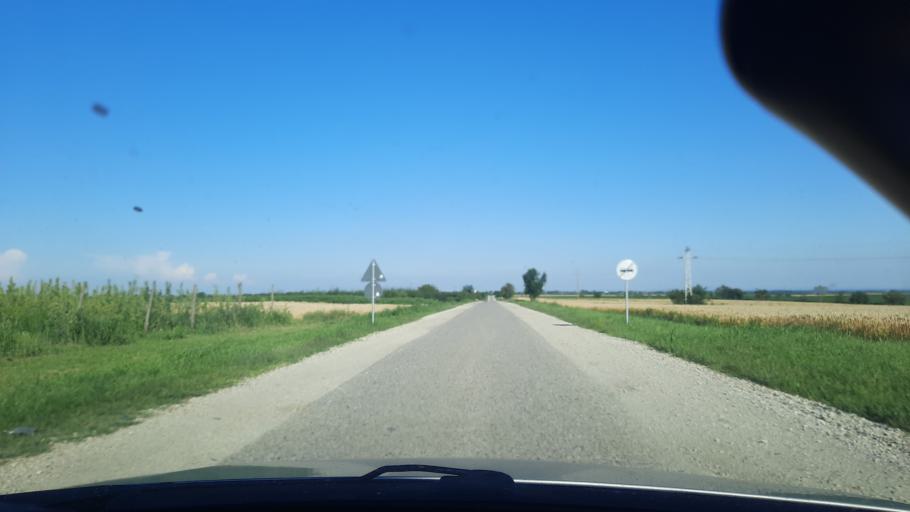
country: RS
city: Cortanovci
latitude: 45.1141
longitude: 19.9638
